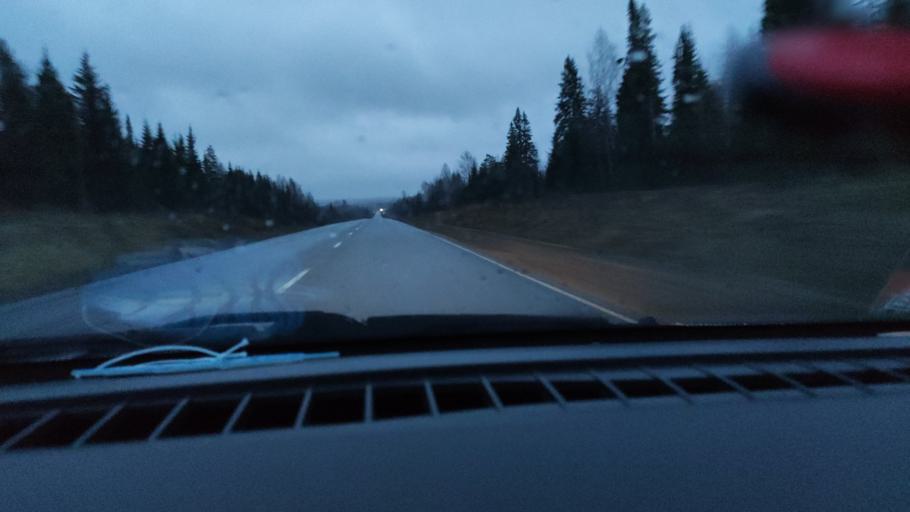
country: RU
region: Udmurtiya
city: Mozhga
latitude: 56.3311
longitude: 52.3062
